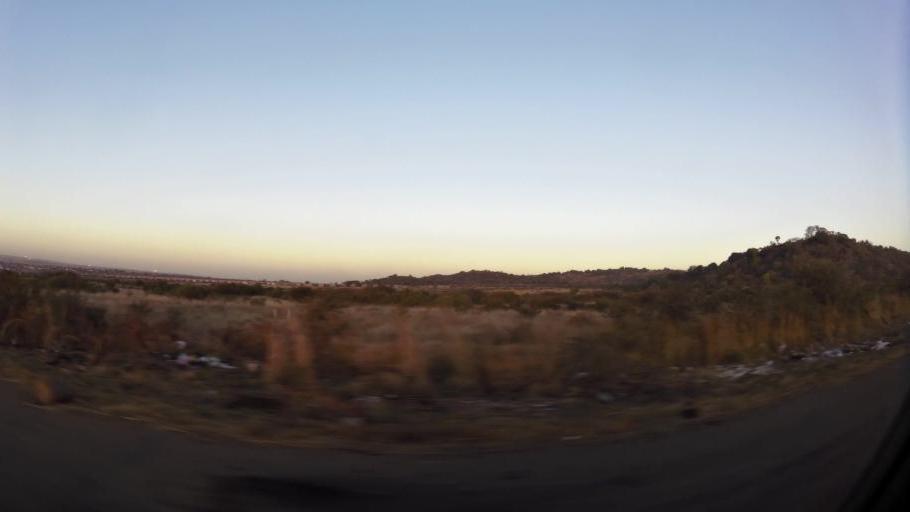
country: ZA
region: North-West
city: Ga-Rankuwa
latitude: -25.5986
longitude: 28.0407
